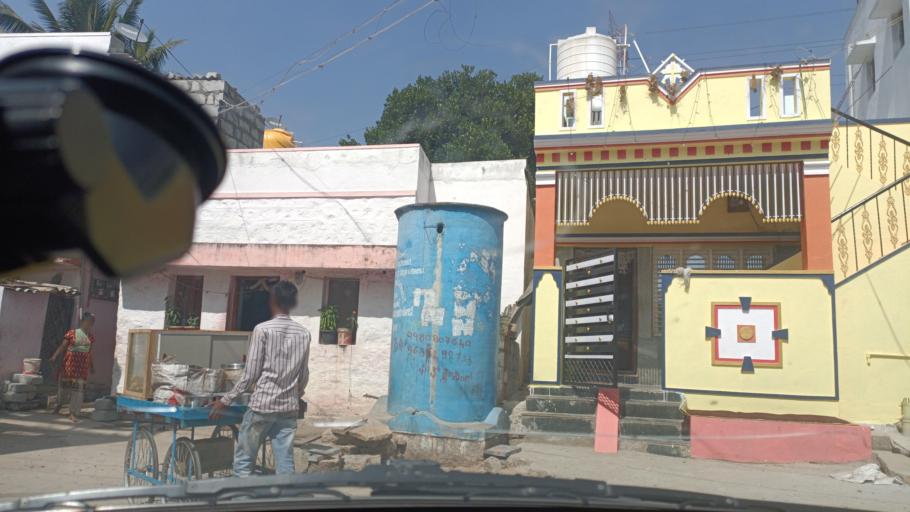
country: IN
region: Karnataka
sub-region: Bangalore Rural
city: Devanhalli
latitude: 13.1838
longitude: 77.6430
